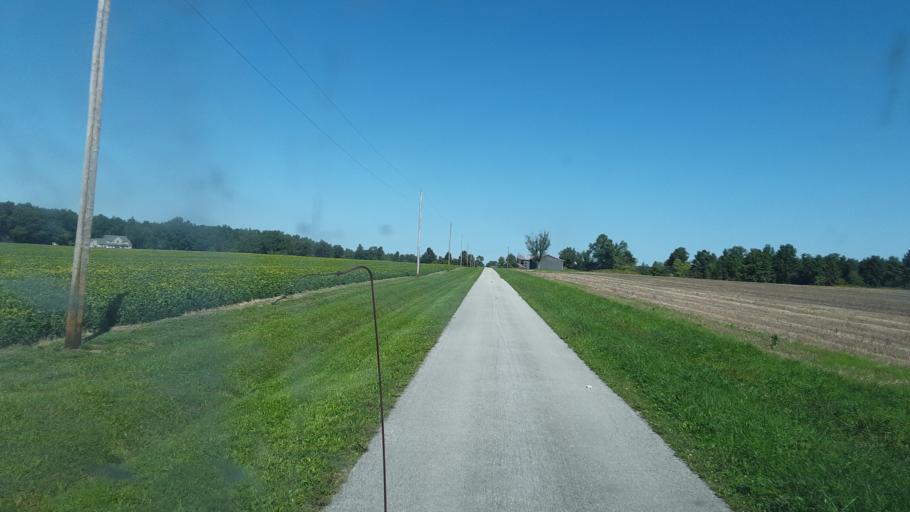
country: US
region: Ohio
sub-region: Sandusky County
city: Mount Carmel
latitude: 41.1477
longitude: -82.9189
